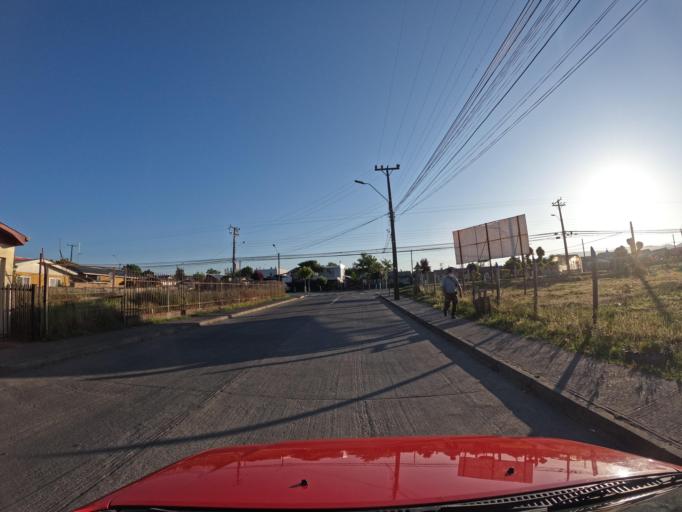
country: CL
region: Biobio
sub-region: Provincia de Concepcion
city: Lota
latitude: -37.1688
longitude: -72.9474
